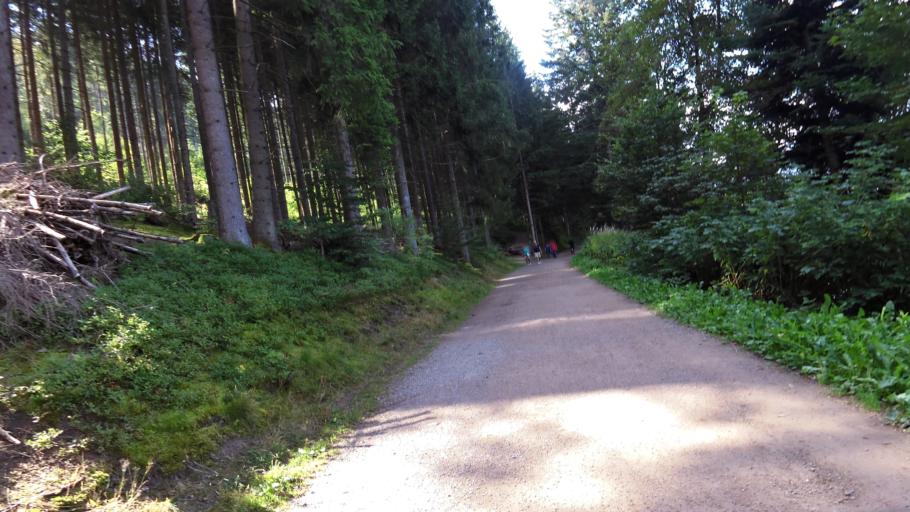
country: DE
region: Baden-Wuerttemberg
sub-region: Freiburg Region
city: Hinterzarten
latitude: 47.8889
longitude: 8.1449
